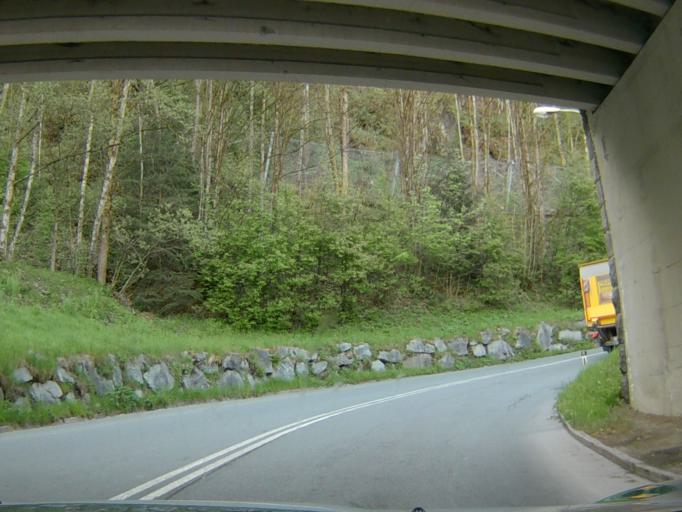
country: AT
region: Salzburg
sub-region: Politischer Bezirk Zell am See
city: Mittersill
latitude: 47.2736
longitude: 12.4849
